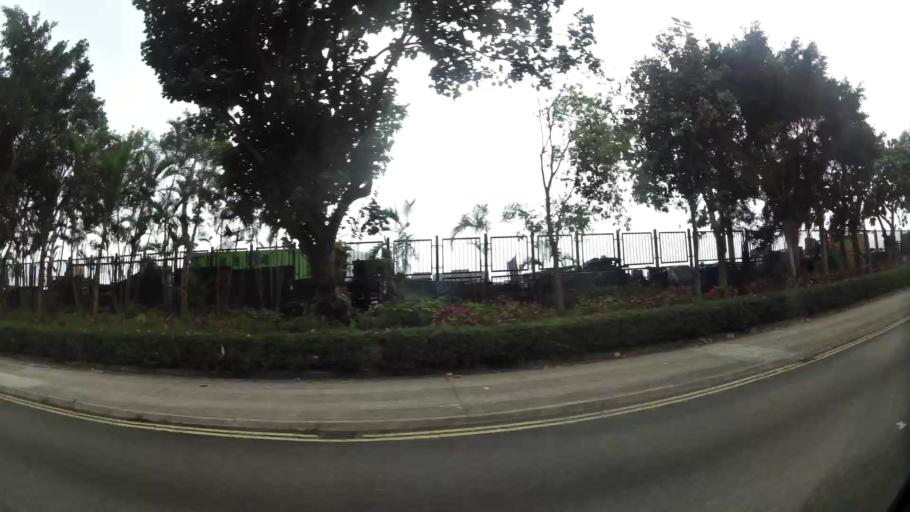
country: HK
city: Hong Kong
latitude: 22.2870
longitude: 114.1318
